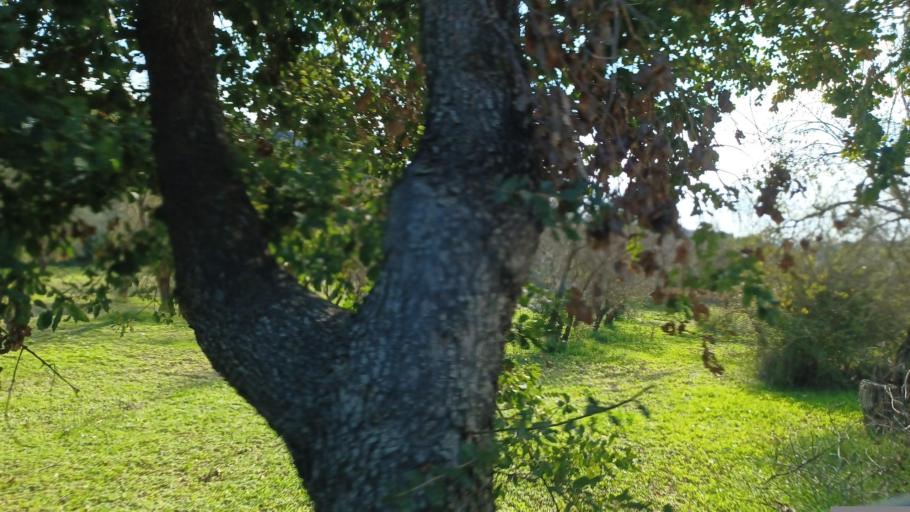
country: CY
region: Pafos
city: Mesogi
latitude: 34.8525
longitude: 32.5099
